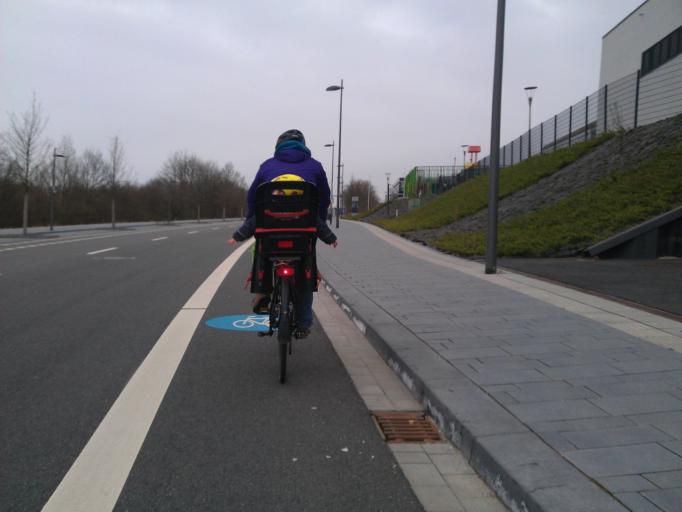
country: DE
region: North Rhine-Westphalia
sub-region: Regierungsbezirk Koln
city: Aachen
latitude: 50.7860
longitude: 6.0506
